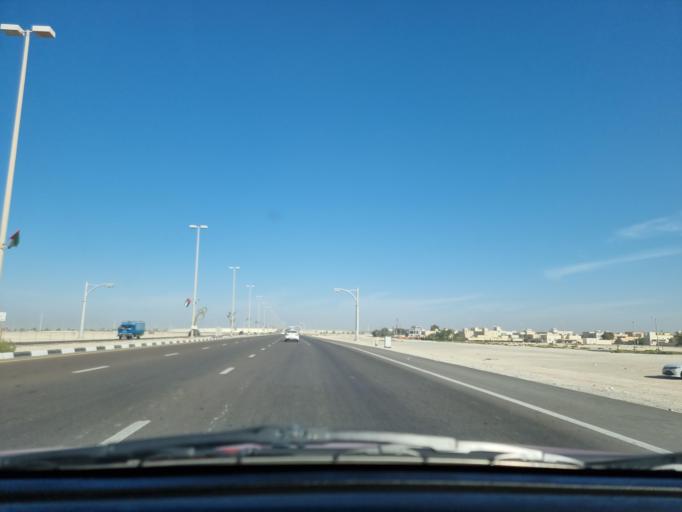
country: AE
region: Abu Dhabi
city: Abu Dhabi
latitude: 24.4036
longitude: 54.7167
